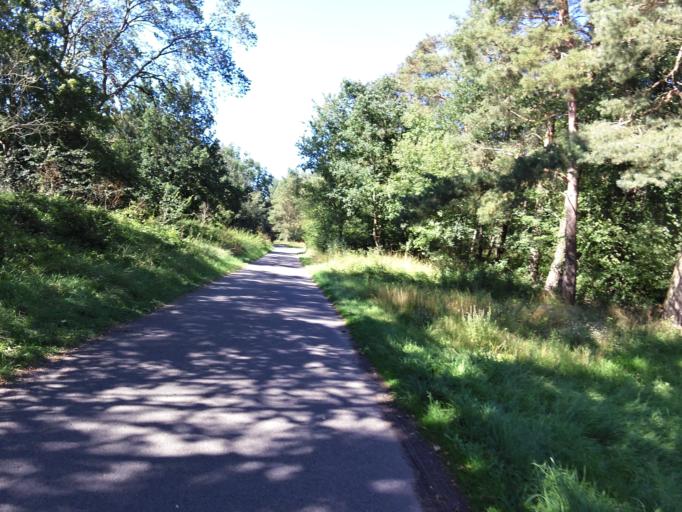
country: DE
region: Saxony-Anhalt
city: Muhlanger
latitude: 51.8528
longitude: 12.7218
